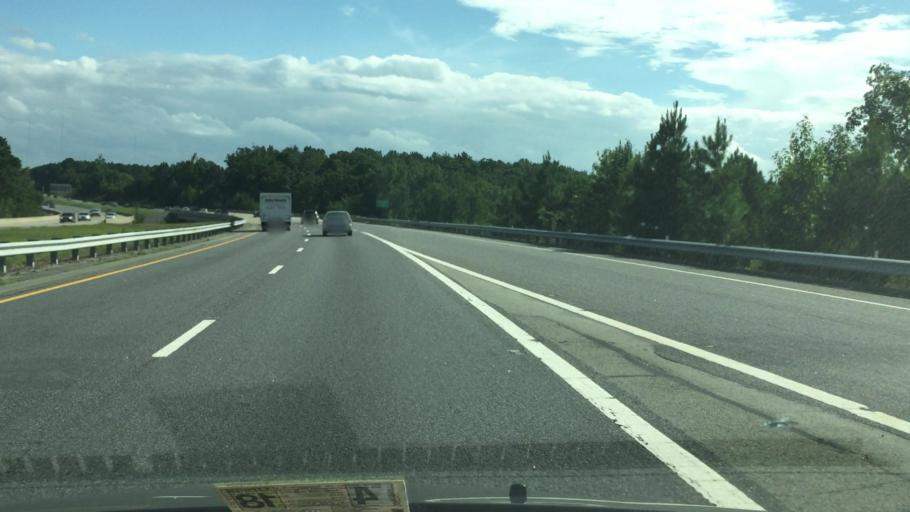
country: US
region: Virginia
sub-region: Henrico County
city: Short Pump
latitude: 37.5547
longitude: -77.6937
